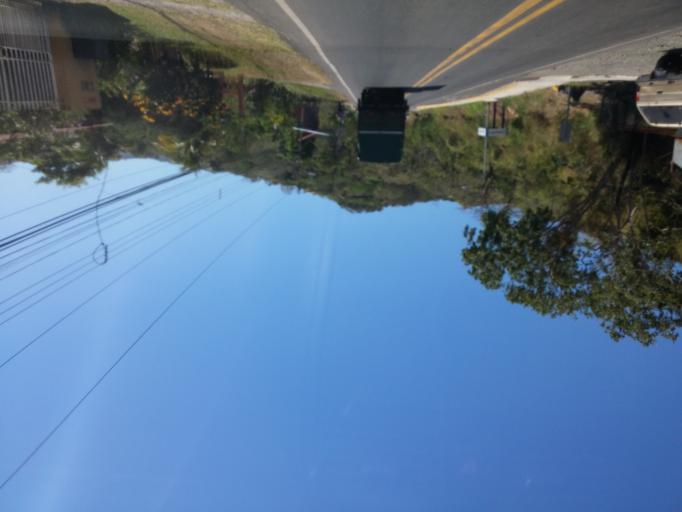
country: CR
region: Heredia
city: Colon
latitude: 9.9067
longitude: -84.2376
